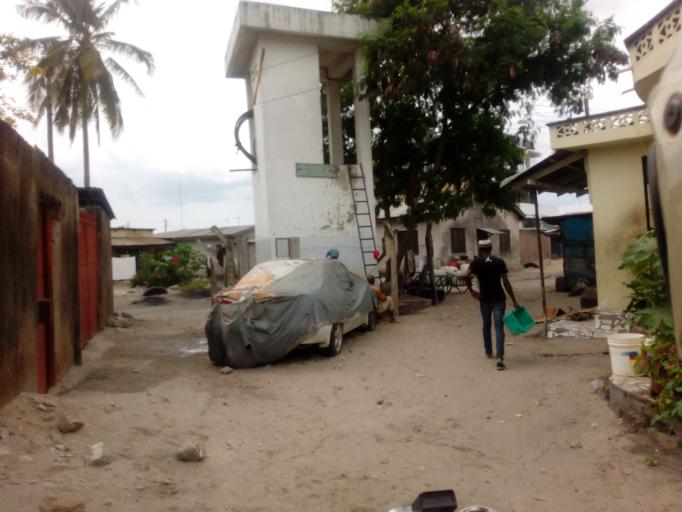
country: TZ
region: Dar es Salaam
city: Dar es Salaam
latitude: -6.8528
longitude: 39.2556
